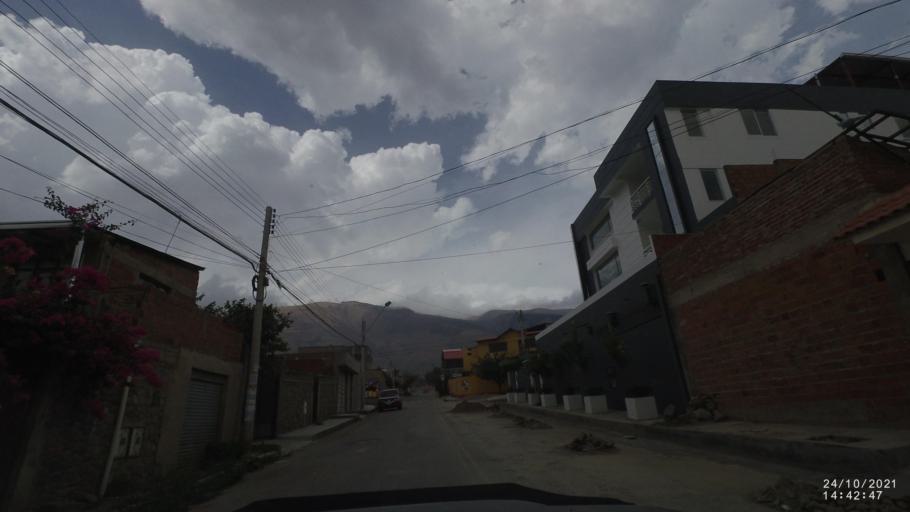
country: BO
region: Cochabamba
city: Cochabamba
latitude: -17.3504
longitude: -66.1772
